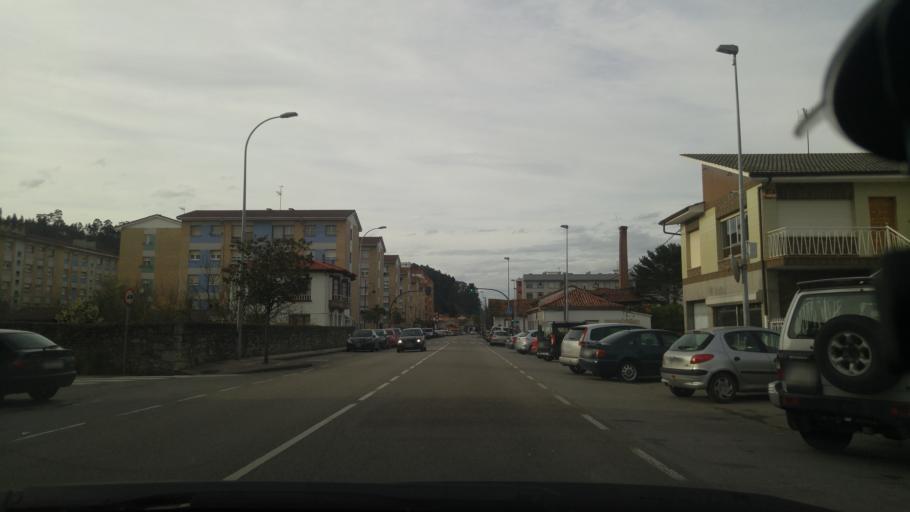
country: ES
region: Asturias
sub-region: Province of Asturias
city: Corvera de Asturias
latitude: 43.5095
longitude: -5.8680
